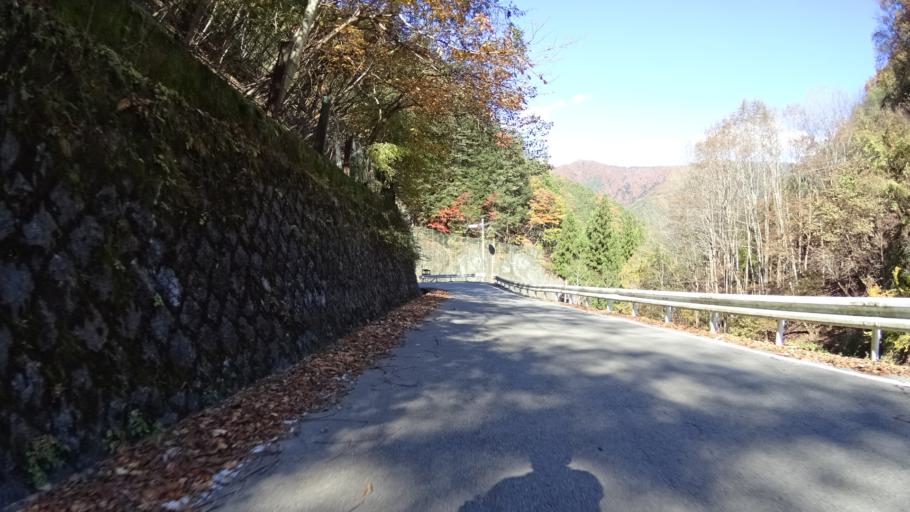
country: JP
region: Yamanashi
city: Otsuki
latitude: 35.7778
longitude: 138.9209
